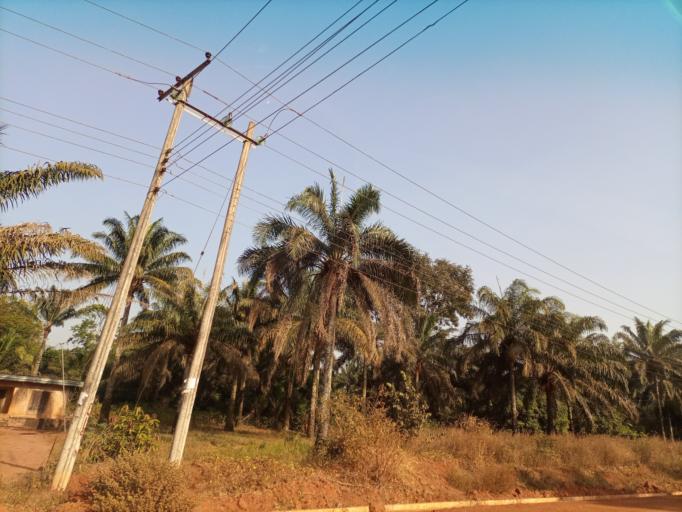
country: NG
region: Enugu
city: Opi
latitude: 6.7784
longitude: 7.3893
